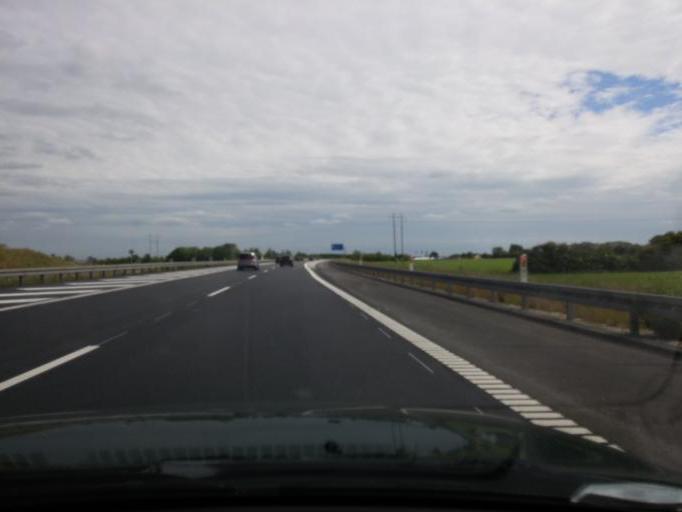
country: DK
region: South Denmark
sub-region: Middelfart Kommune
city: Norre Aby
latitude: 55.4736
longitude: 9.8907
